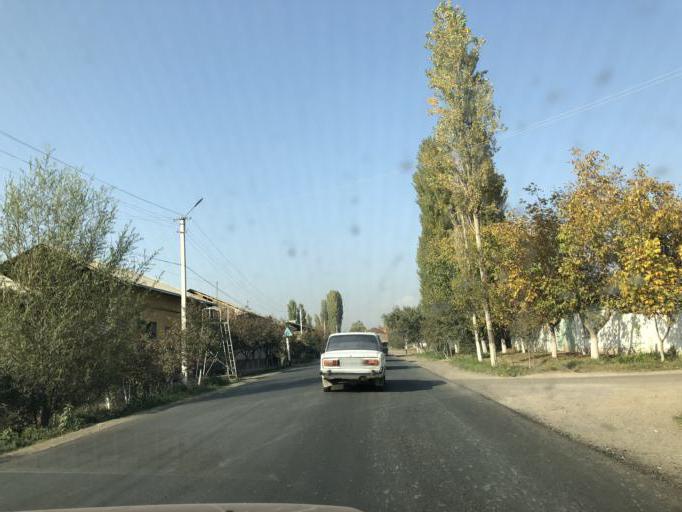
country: UZ
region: Namangan
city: Chust Shahri
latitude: 41.0689
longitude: 71.2046
